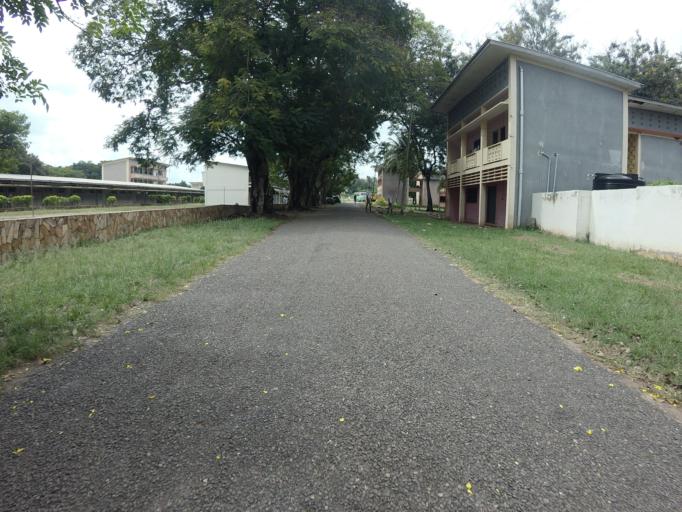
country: GH
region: Volta
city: Ho
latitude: 6.5964
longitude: 0.4751
